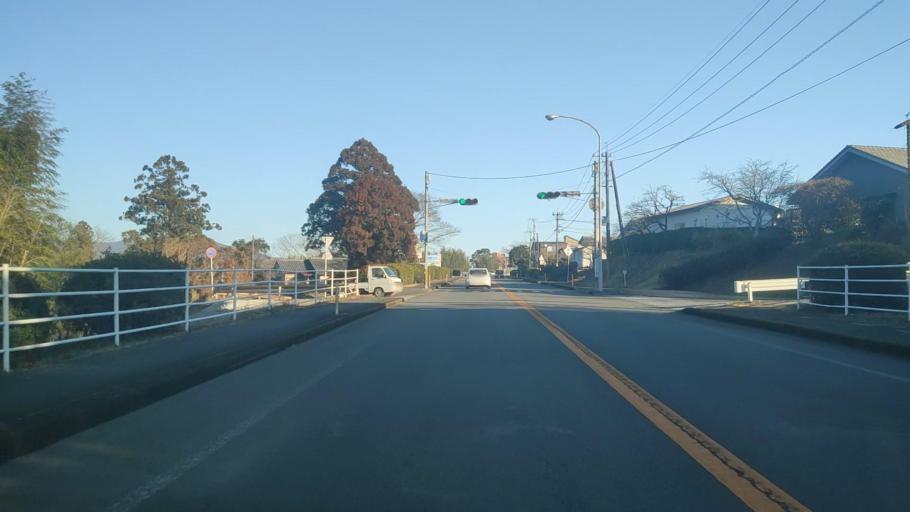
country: JP
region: Miyazaki
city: Takanabe
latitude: 32.1916
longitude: 131.5242
